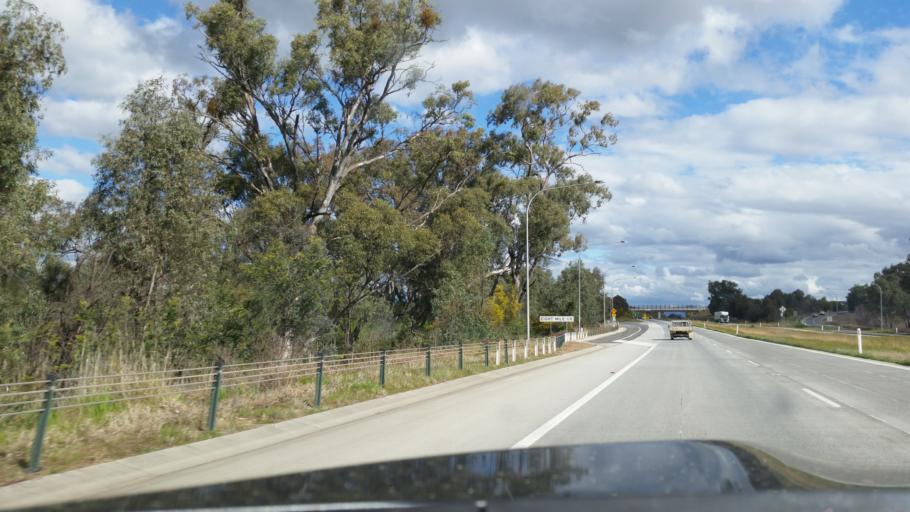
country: AU
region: New South Wales
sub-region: Albury Municipality
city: Lavington
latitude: -35.9968
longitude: 146.9931
